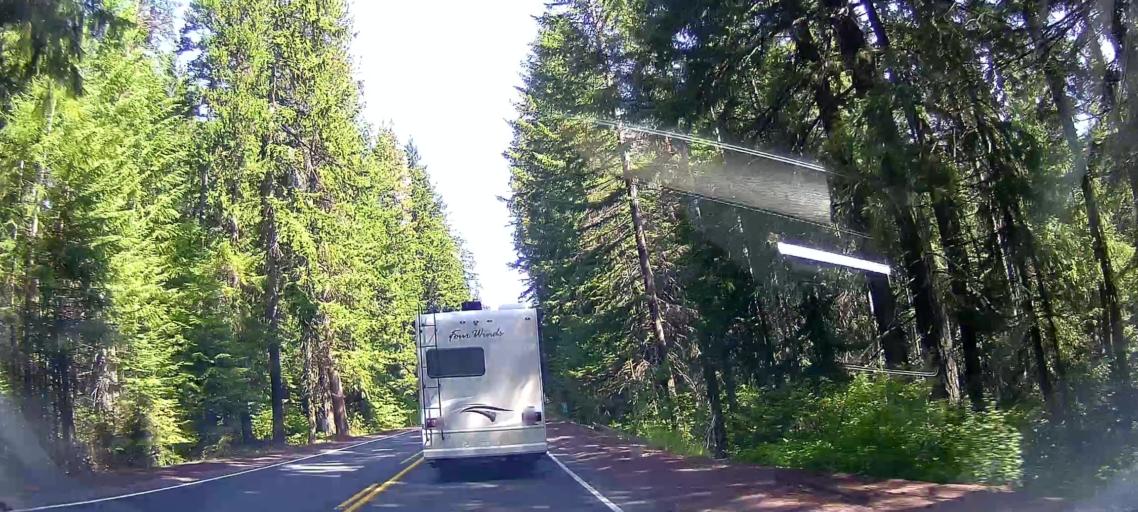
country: US
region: Oregon
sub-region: Jefferson County
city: Warm Springs
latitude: 45.0838
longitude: -121.5434
